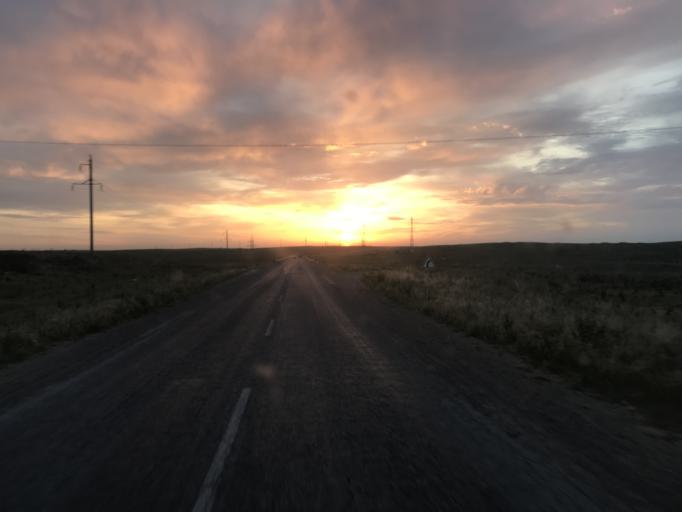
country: UZ
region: Toshkent
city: Chinoz
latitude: 41.0856
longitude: 68.6635
